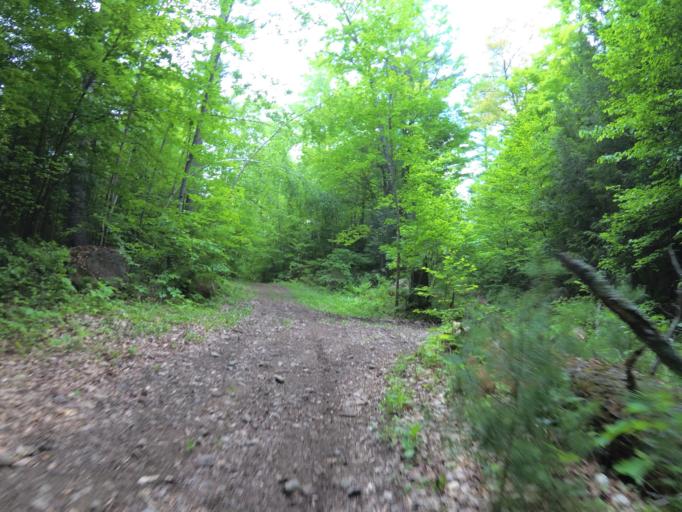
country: CA
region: Ontario
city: Renfrew
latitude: 45.0573
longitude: -76.8680
